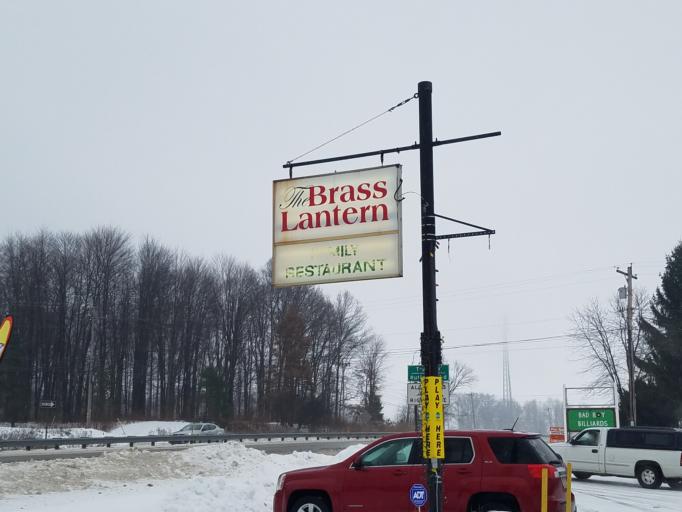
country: US
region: Pennsylvania
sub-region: Mercer County
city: Reynolds Heights
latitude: 41.3273
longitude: -80.4122
